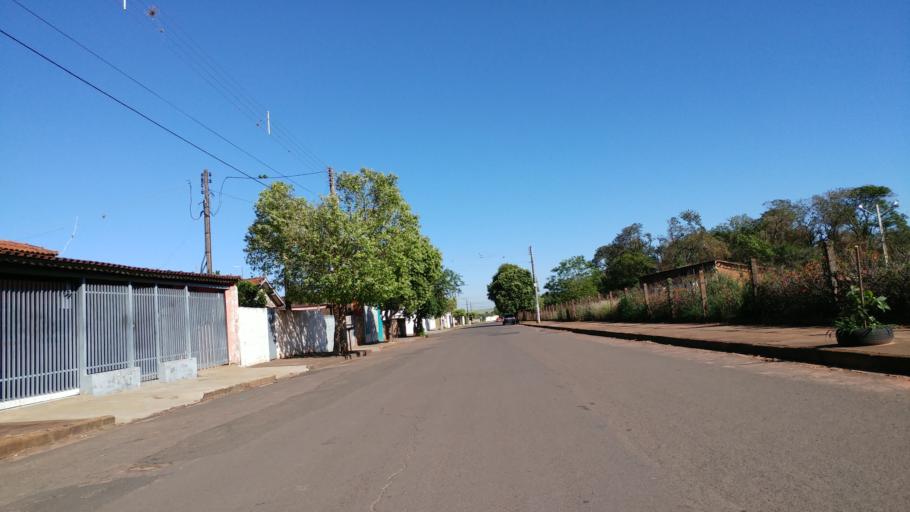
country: BR
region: Sao Paulo
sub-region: Paraguacu Paulista
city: Paraguacu Paulista
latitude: -22.4189
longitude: -50.5834
